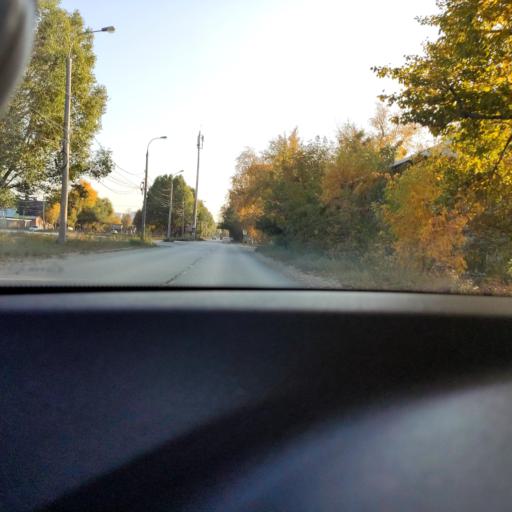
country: RU
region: Samara
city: Petra-Dubrava
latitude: 53.2379
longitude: 50.3076
